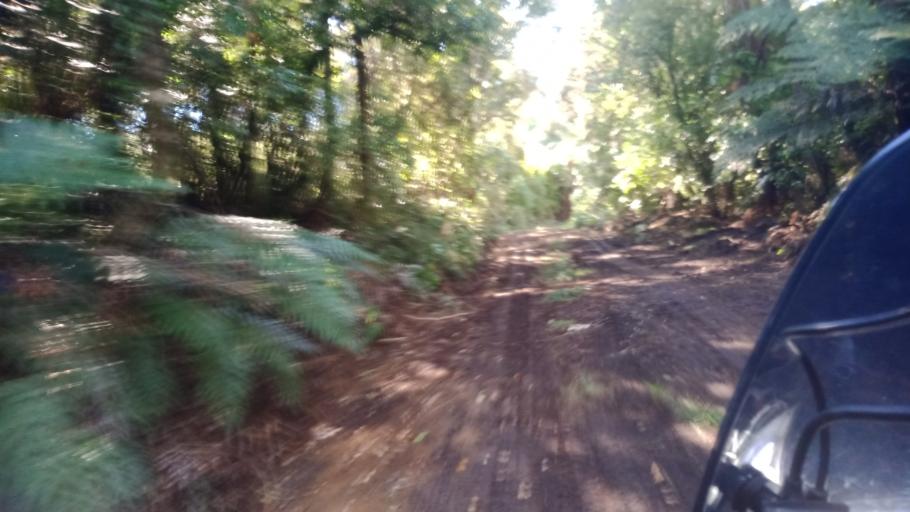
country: NZ
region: Hawke's Bay
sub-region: Wairoa District
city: Wairoa
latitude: -39.0034
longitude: 177.0573
